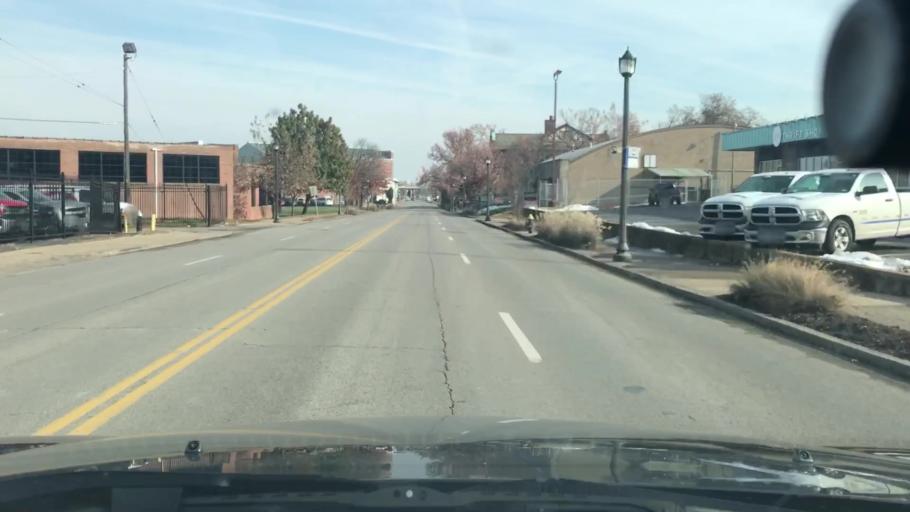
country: US
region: Missouri
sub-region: Saint Louis County
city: Richmond Heights
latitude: 38.6142
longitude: -90.2655
